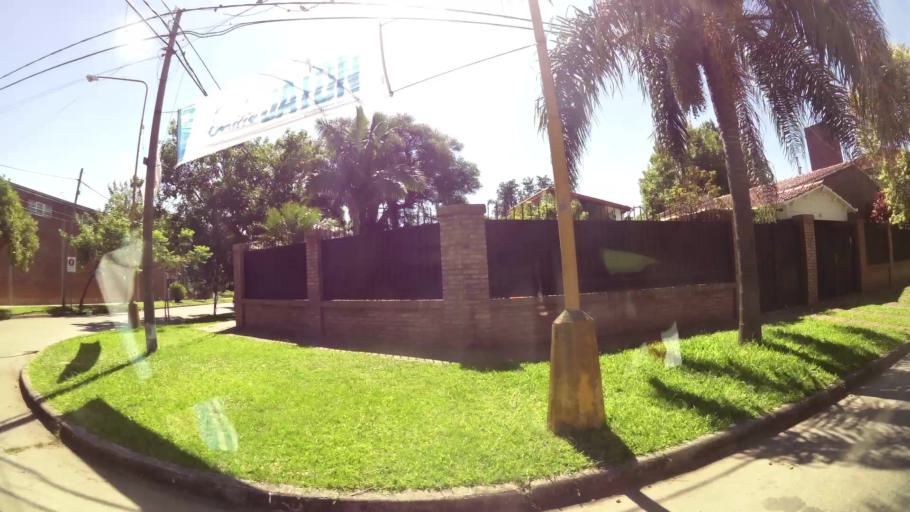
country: AR
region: Santa Fe
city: Santa Fe de la Vera Cruz
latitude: -31.6071
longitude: -60.6686
